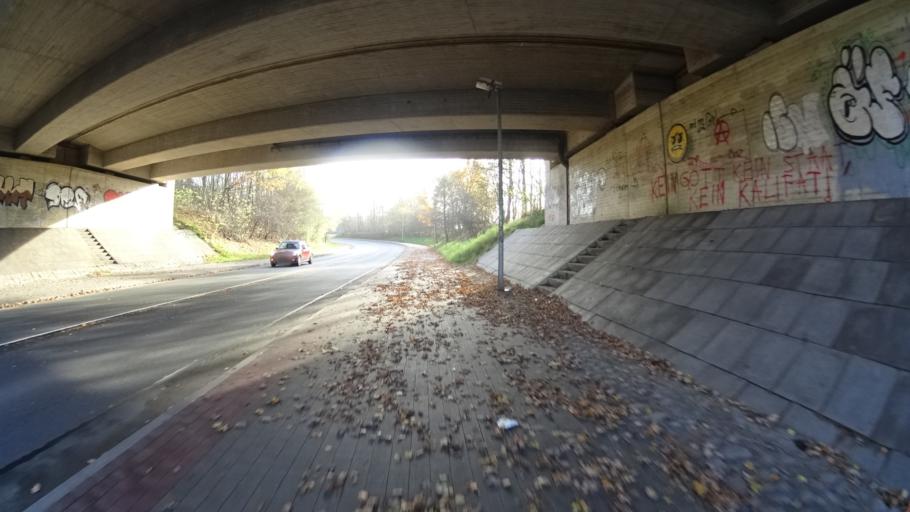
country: DE
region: Lower Saxony
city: Wendisch Evern
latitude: 53.2414
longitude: 10.4595
